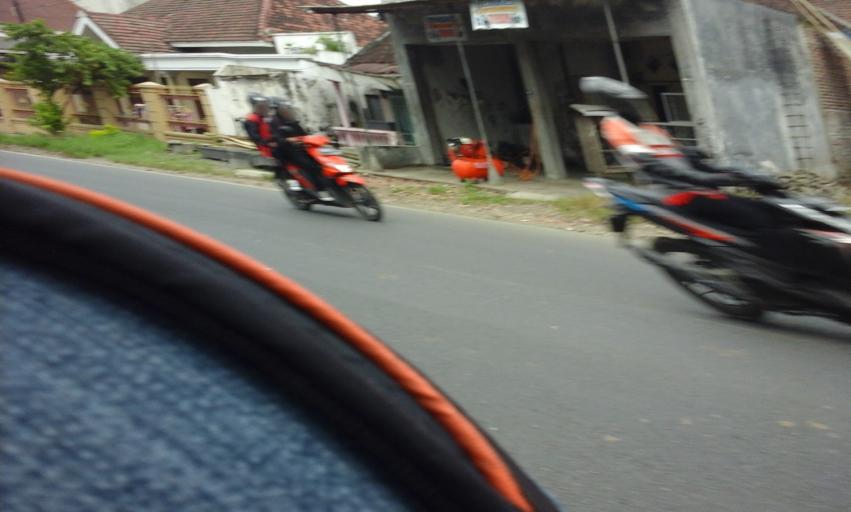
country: ID
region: East Java
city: Dukuhsia
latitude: -8.2021
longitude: 113.6186
